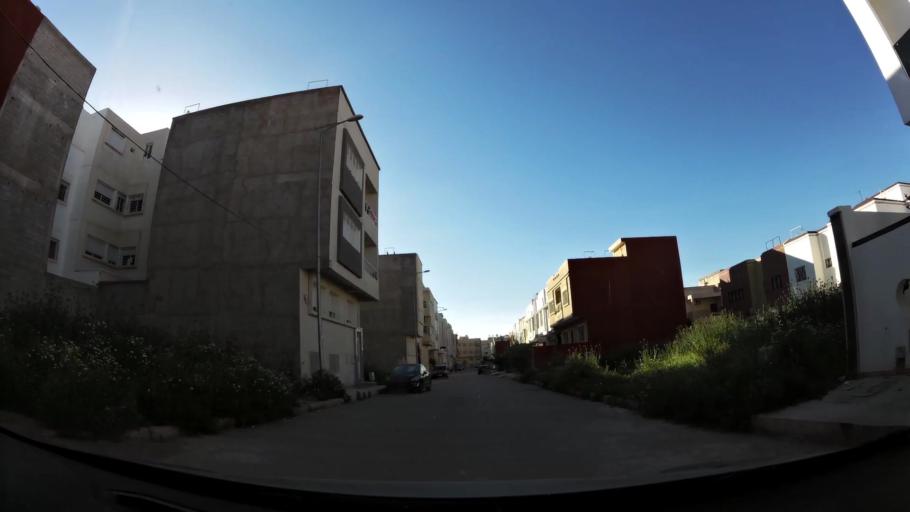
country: MA
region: Fes-Boulemane
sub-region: Fes
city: Fes
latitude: 34.0092
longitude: -5.0113
